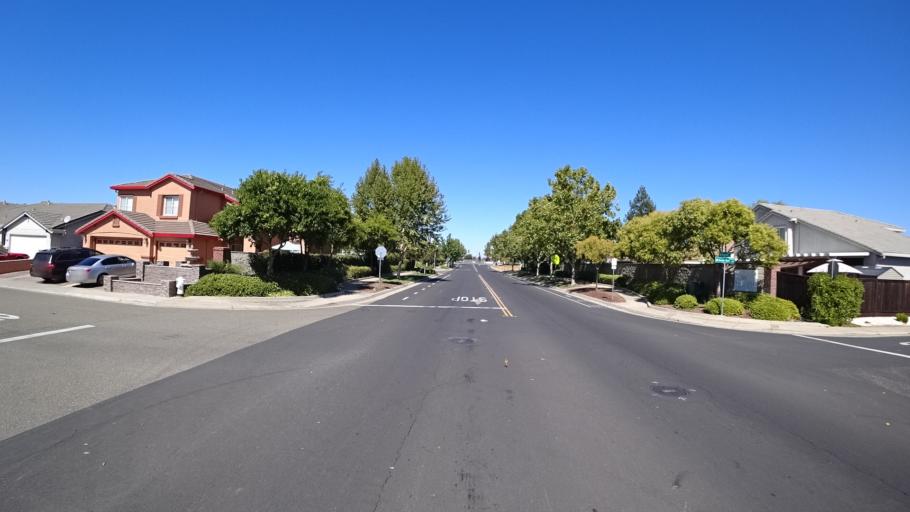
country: US
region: California
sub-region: Sacramento County
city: Elk Grove
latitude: 38.4218
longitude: -121.3435
